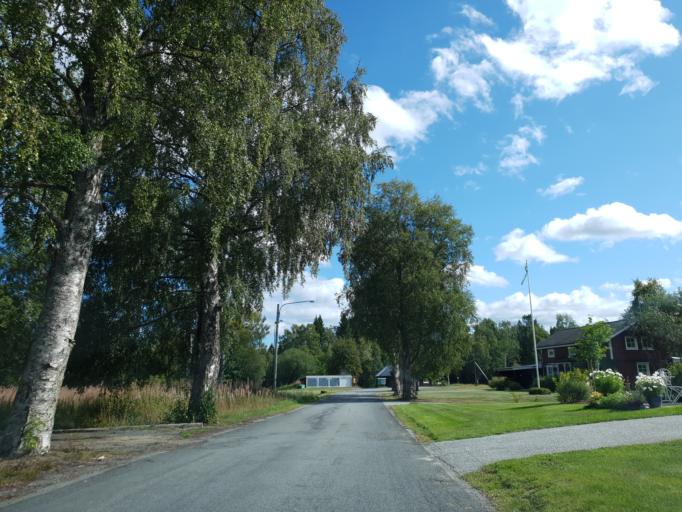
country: SE
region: Vaesternorrland
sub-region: OErnskoeldsviks Kommun
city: Husum
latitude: 63.3403
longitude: 19.1142
